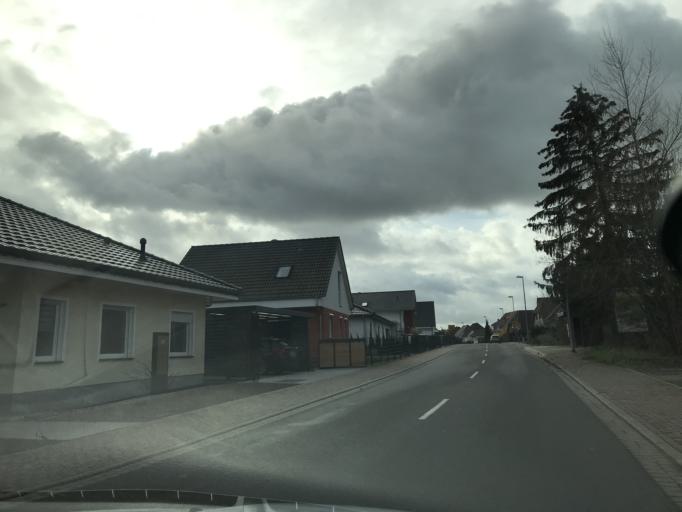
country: DE
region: Saxony
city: Delitzsch
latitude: 51.5348
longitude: 12.3123
